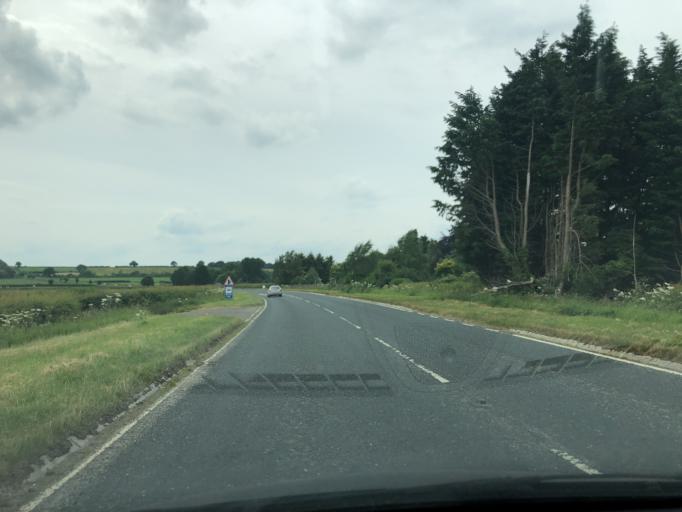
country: GB
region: England
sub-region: North Yorkshire
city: Pickering
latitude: 54.2631
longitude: -0.8248
